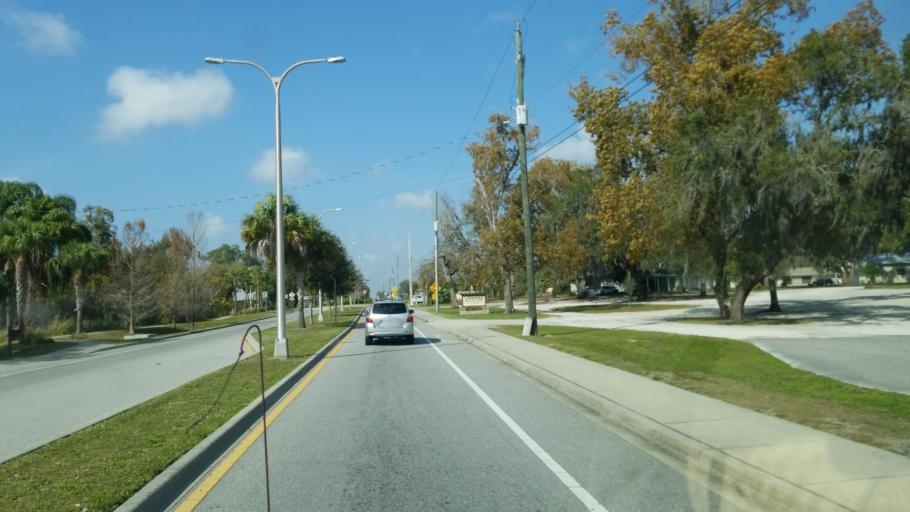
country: US
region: Florida
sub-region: Sarasota County
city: Fruitville
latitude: 27.3253
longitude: -82.4638
